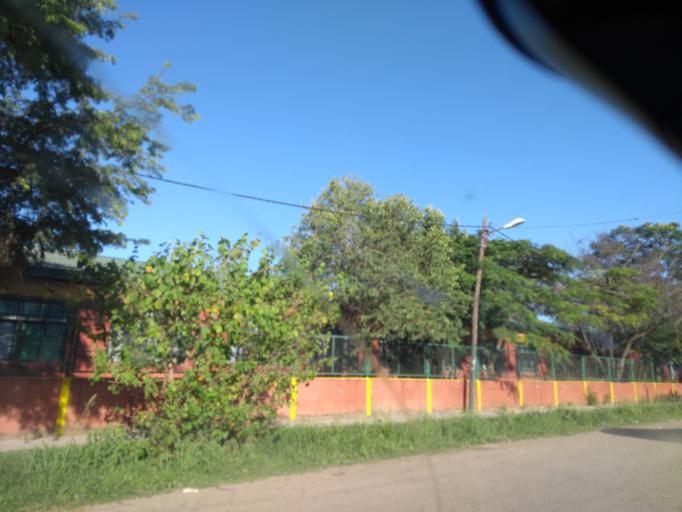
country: AR
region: Chaco
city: Resistencia
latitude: -27.4733
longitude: -58.9722
